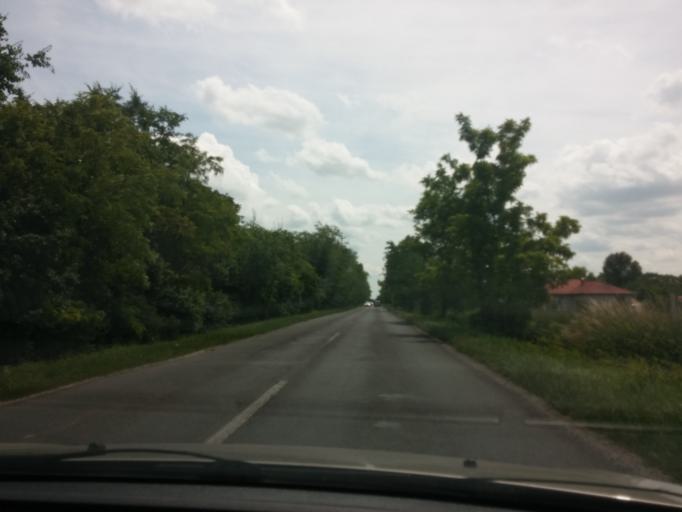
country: HU
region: Pest
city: Szigetcsep
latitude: 47.2892
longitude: 18.9823
